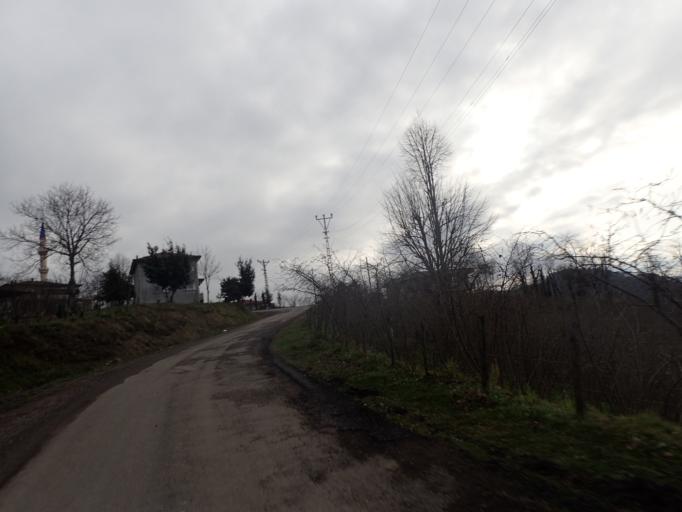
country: TR
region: Ordu
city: Camas
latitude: 40.9320
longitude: 37.5178
